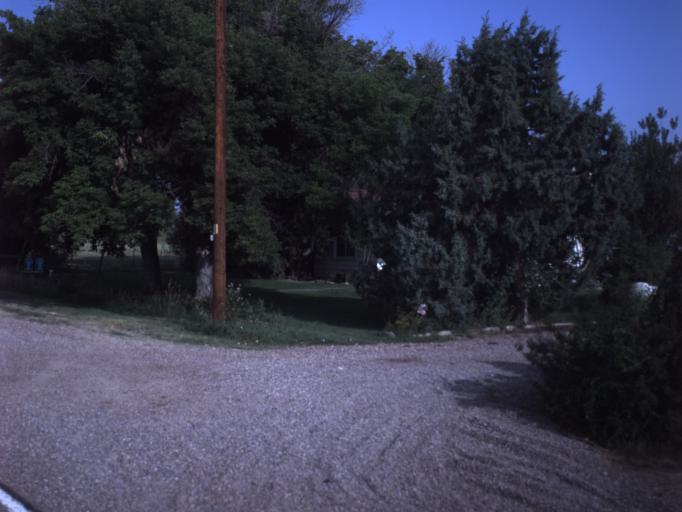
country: US
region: Utah
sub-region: Duchesne County
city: Roosevelt
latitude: 40.2584
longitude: -110.1096
